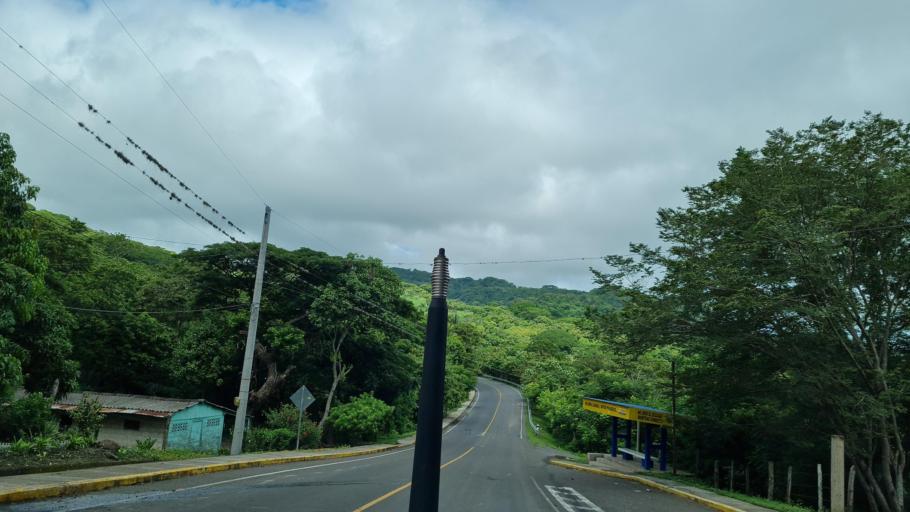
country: NI
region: Matagalpa
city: Terrabona
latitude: 12.5913
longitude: -85.9112
